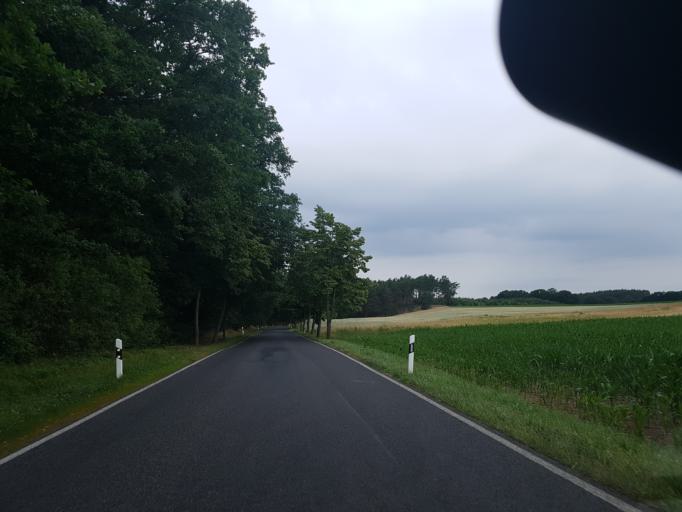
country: DE
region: Brandenburg
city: Hohenbucko
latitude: 51.7003
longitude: 13.4995
